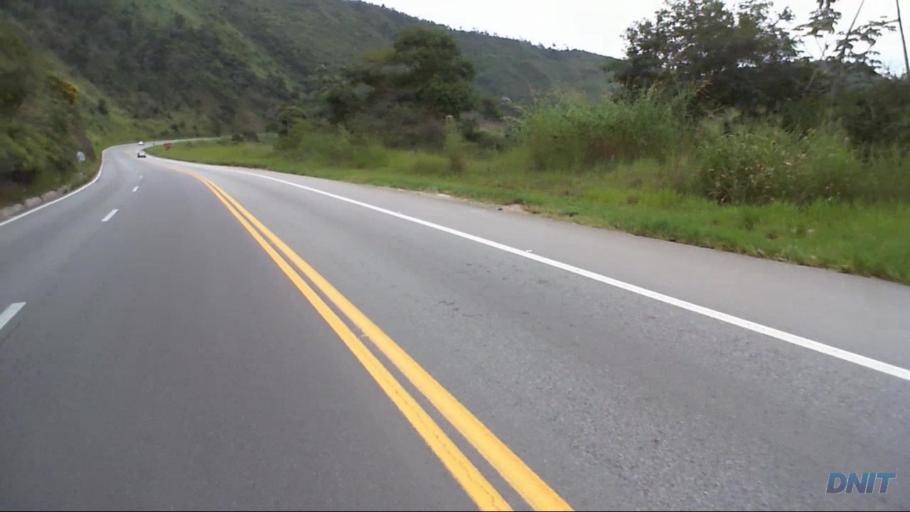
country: BR
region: Minas Gerais
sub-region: Nova Era
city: Nova Era
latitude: -19.6377
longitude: -42.8989
